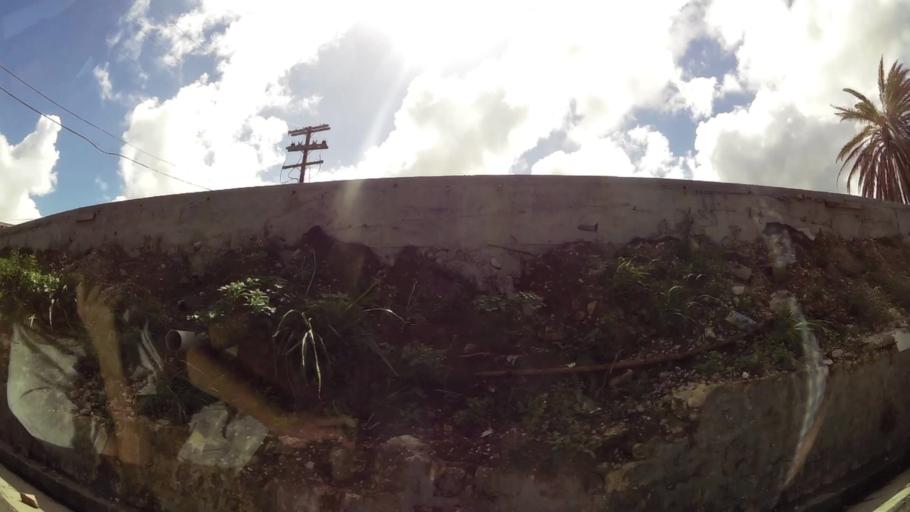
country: AG
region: Saint John
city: Saint John's
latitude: 17.1183
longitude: -61.8388
